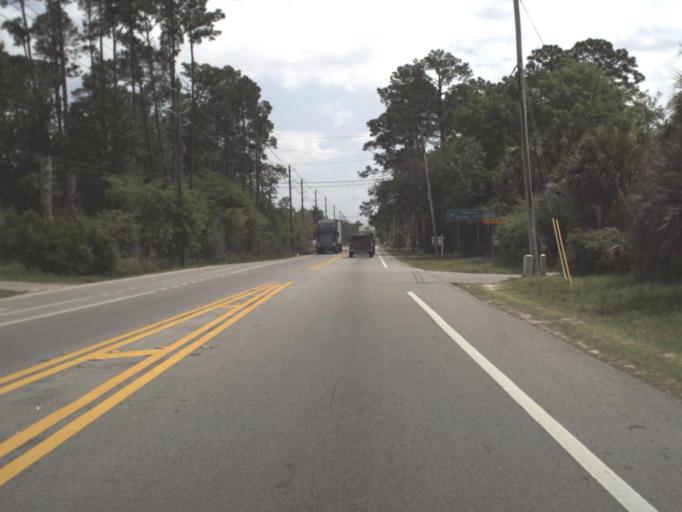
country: US
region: Florida
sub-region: Escambia County
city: Myrtle Grove
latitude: 30.3653
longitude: -87.3433
